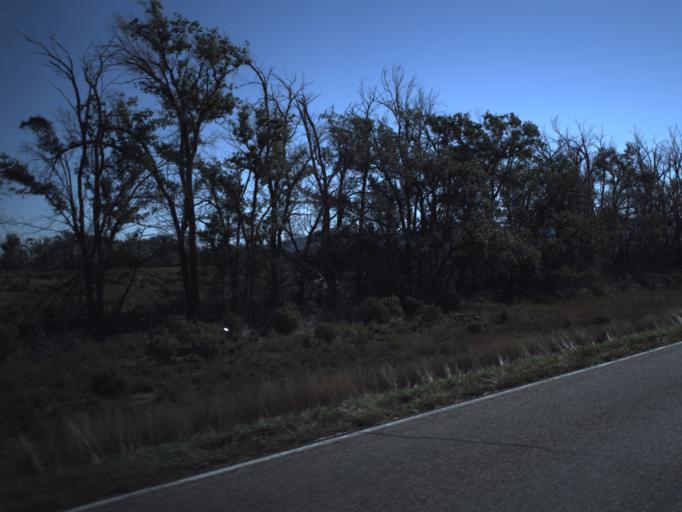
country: US
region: Utah
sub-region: Washington County
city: Enterprise
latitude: 37.7126
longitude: -113.6650
